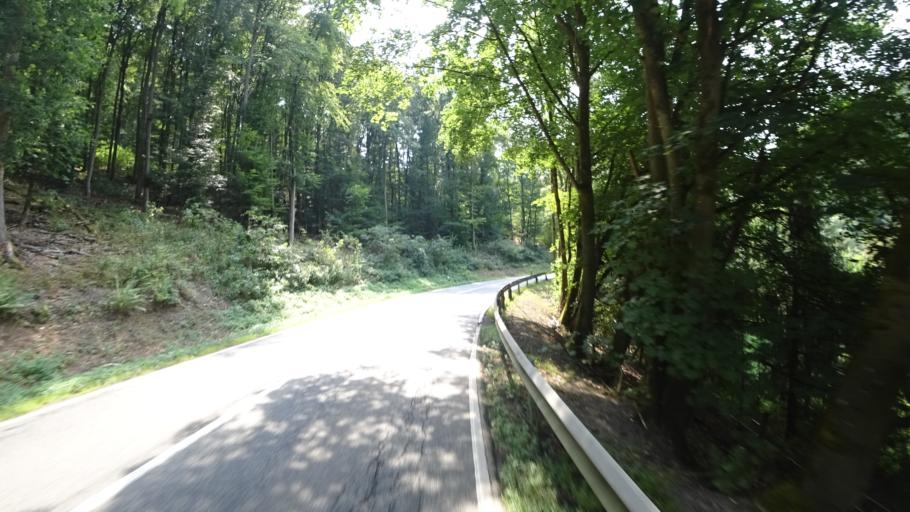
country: DE
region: Rheinland-Pfalz
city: Hohr-Grenzhausen
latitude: 50.4233
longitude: 7.6461
